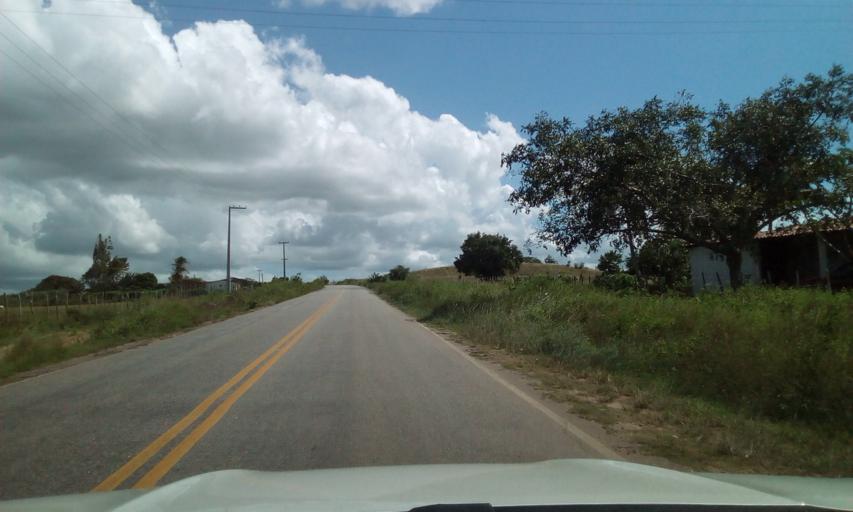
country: BR
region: Paraiba
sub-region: Guarabira
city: Guarabira
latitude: -6.8498
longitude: -35.3919
